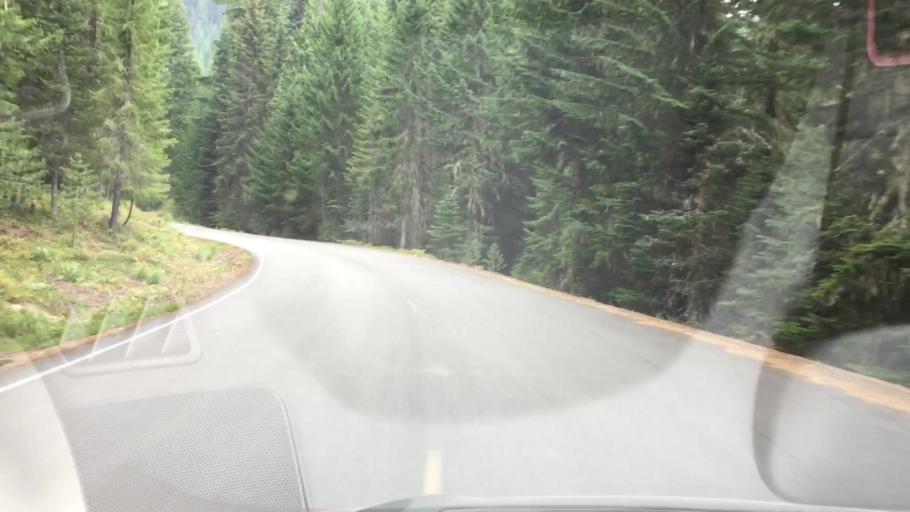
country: US
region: Washington
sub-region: Klickitat County
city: White Salmon
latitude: 46.2283
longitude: -121.6262
